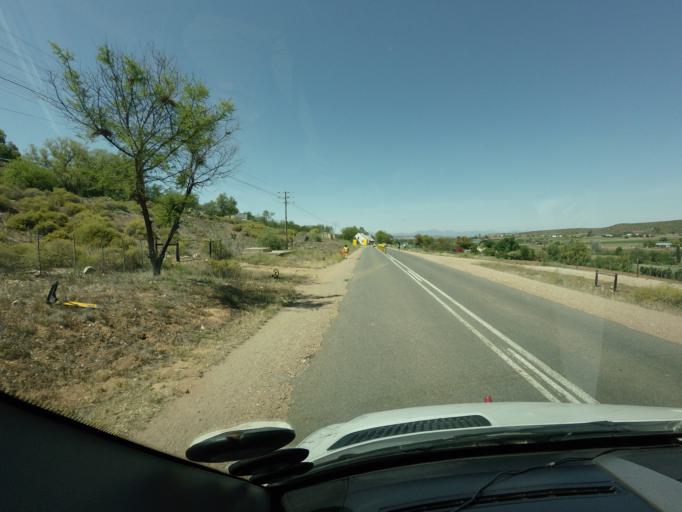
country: ZA
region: Western Cape
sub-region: Eden District Municipality
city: Oudtshoorn
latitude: -33.4814
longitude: 22.2477
